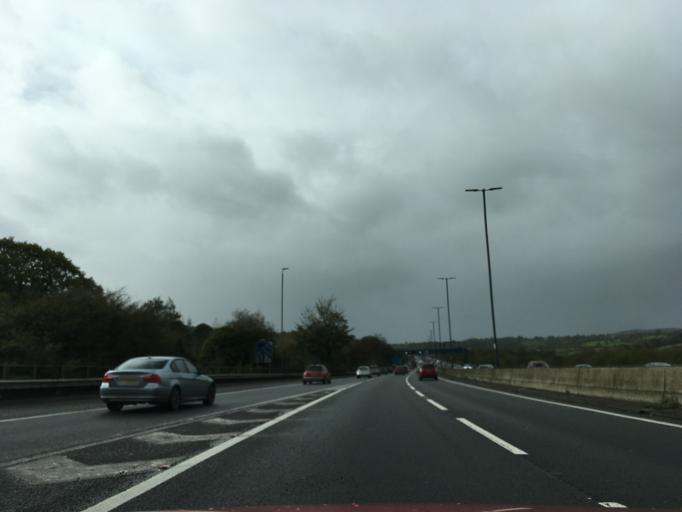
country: GB
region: Wales
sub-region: Newport
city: Newport
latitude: 51.5993
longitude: -3.0081
